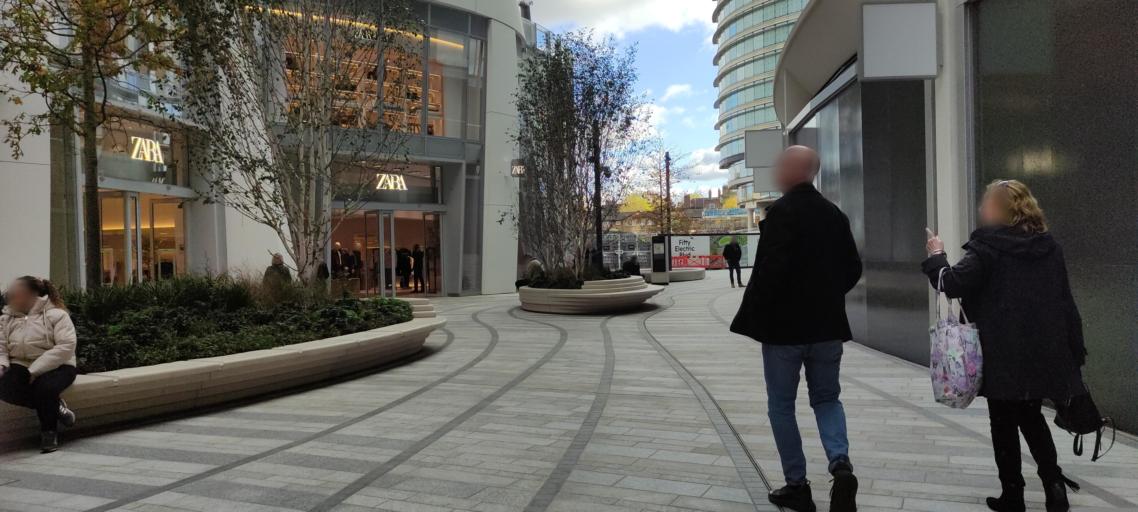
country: GB
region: England
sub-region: Greater London
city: Battersea
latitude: 51.4803
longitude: -0.1448
